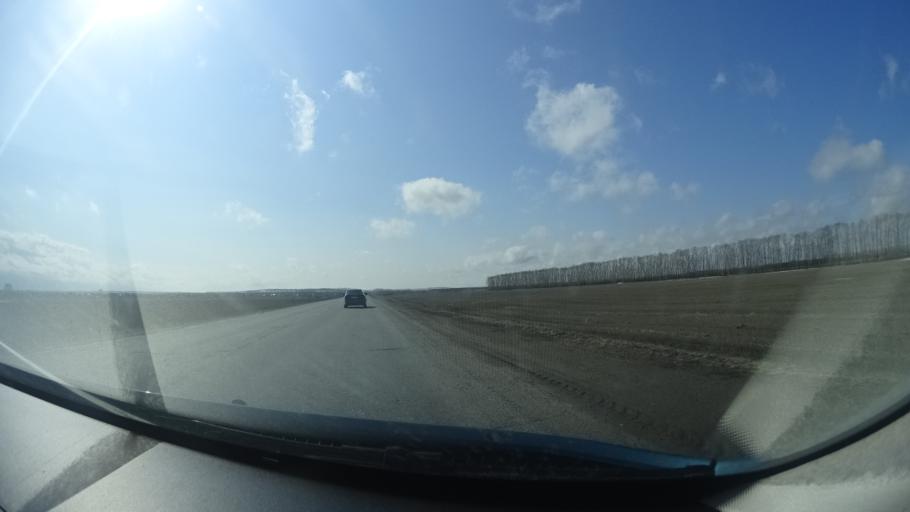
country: RU
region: Bashkortostan
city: Mikhaylovka
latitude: 54.9371
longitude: 55.7454
